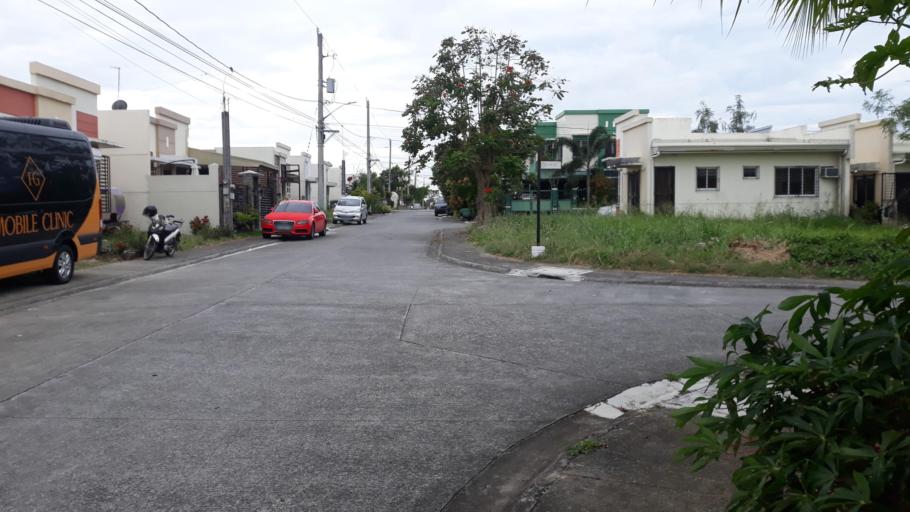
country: PH
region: Calabarzon
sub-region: Province of Cavite
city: Biga
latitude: 14.2741
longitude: 120.9695
